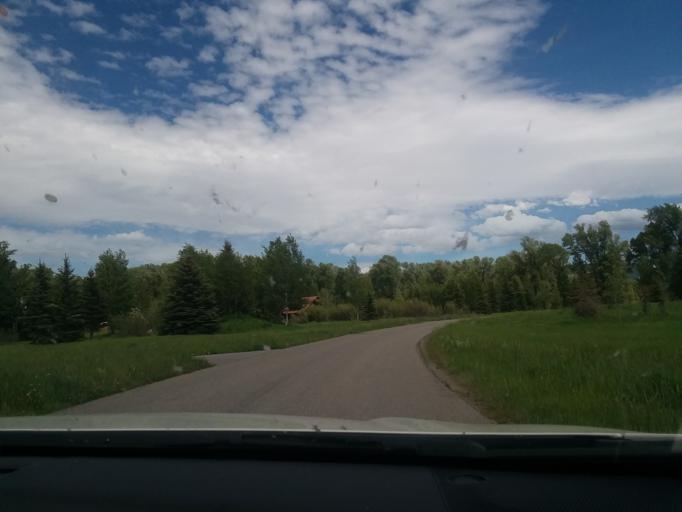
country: US
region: Wyoming
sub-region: Teton County
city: Moose Wilson Road
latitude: 43.5046
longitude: -110.8508
